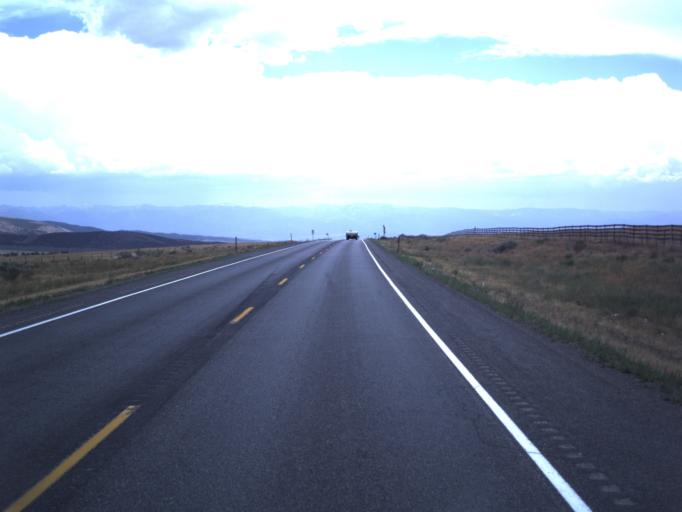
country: US
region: Utah
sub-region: Sanpete County
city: Fountain Green
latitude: 39.6753
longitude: -111.6670
